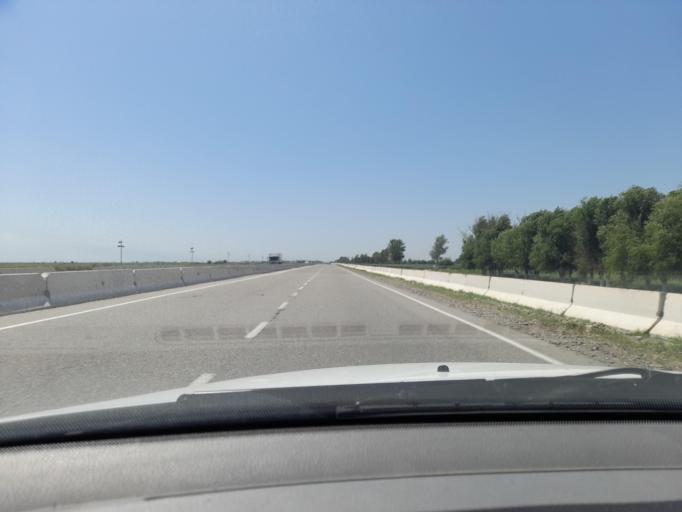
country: UZ
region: Jizzax
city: Paxtakor
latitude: 40.3499
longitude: 68.1300
